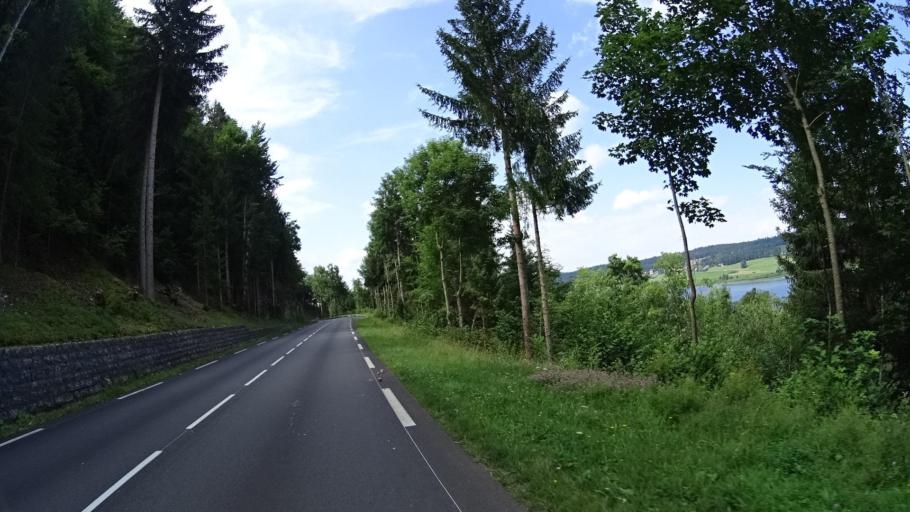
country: FR
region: Franche-Comte
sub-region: Departement du Doubs
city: Les Fourgs
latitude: 46.8289
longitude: 6.3370
